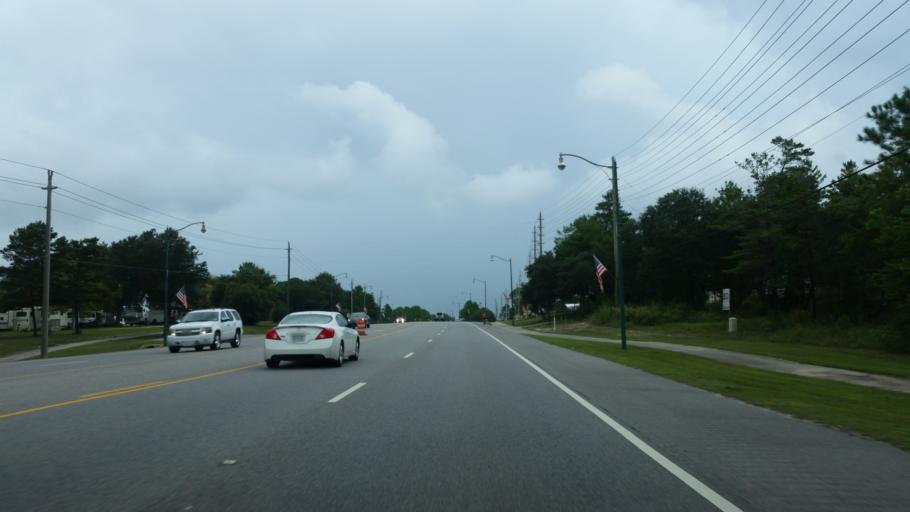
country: US
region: Alabama
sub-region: Baldwin County
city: Orange Beach
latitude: 30.2876
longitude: -87.5814
